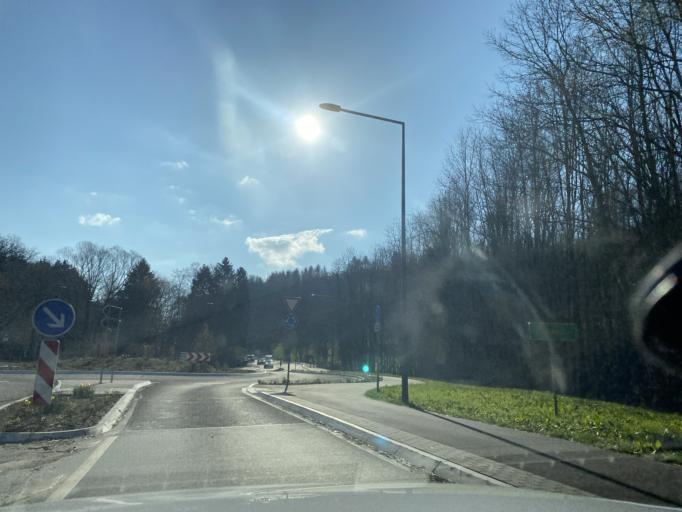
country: DE
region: North Rhine-Westphalia
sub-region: Regierungsbezirk Koln
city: Odenthal
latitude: 51.0270
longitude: 7.1173
